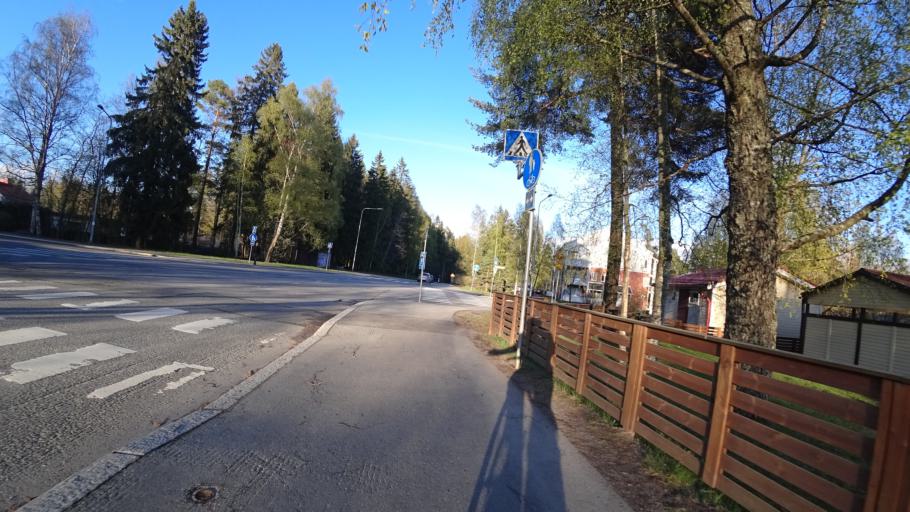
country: FI
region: Pirkanmaa
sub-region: Tampere
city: Pirkkala
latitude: 61.4948
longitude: 23.5854
